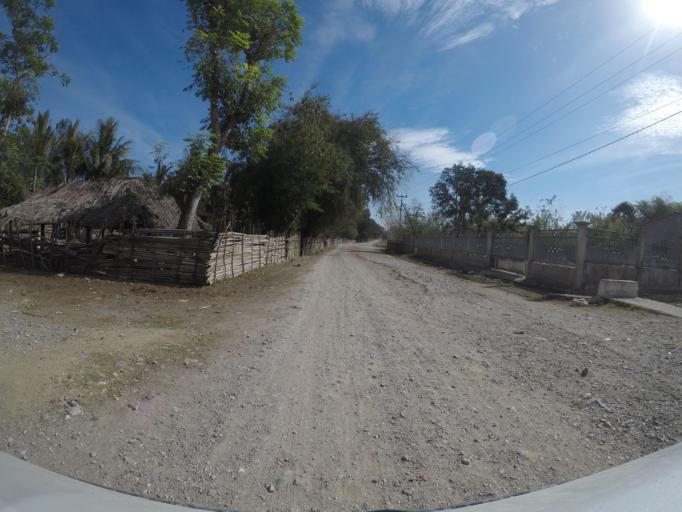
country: TL
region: Bobonaro
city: Maliana
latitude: -8.8721
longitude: 125.2124
